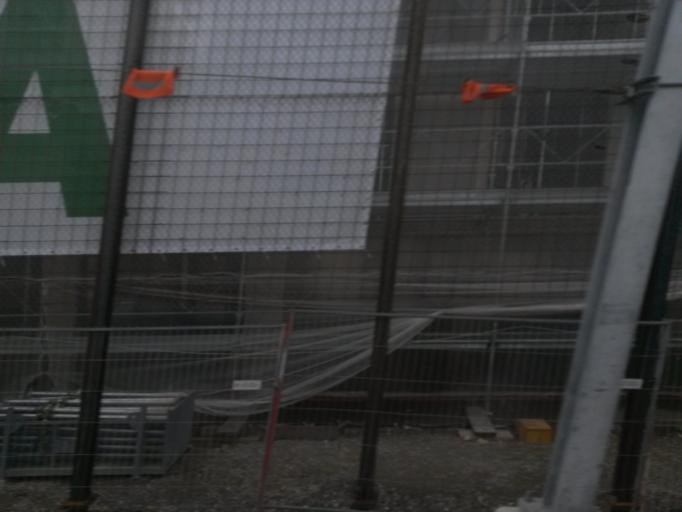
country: CH
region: Vaud
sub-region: Ouest Lausannois District
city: Renens
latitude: 46.5340
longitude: 6.5855
